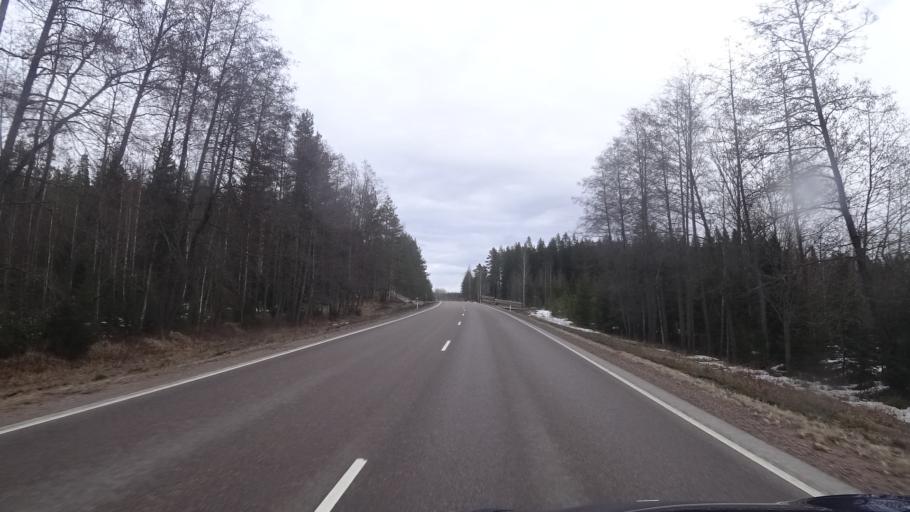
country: FI
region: Kymenlaakso
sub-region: Kouvola
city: Kouvola
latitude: 60.6925
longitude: 26.6527
